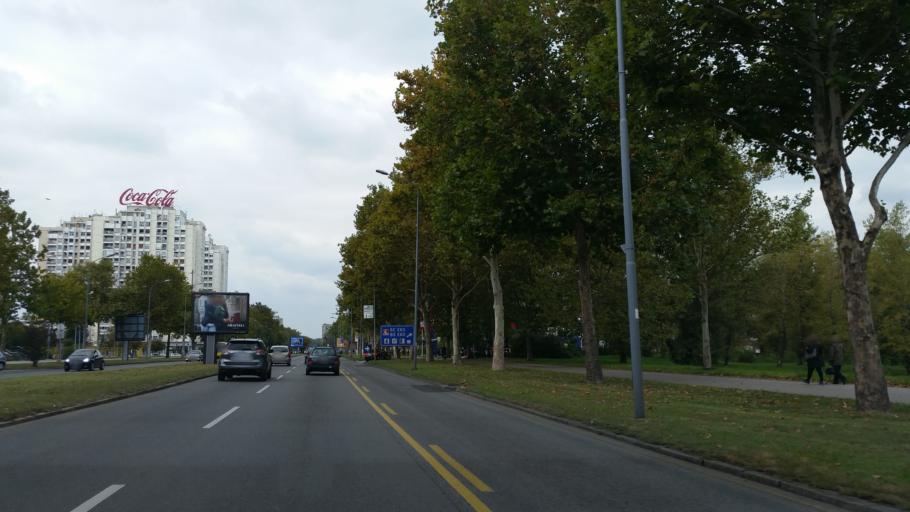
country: RS
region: Central Serbia
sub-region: Belgrade
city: Novi Beograd
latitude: 44.8200
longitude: 20.4229
